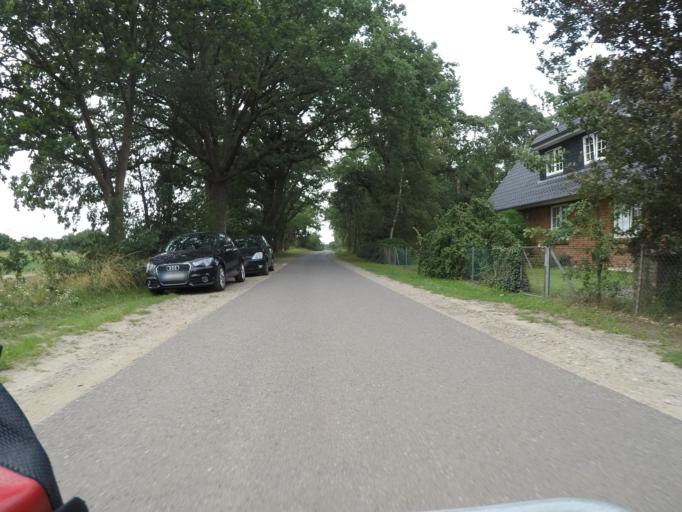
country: DE
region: Lower Saxony
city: Bardowick
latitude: 53.3062
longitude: 10.4035
